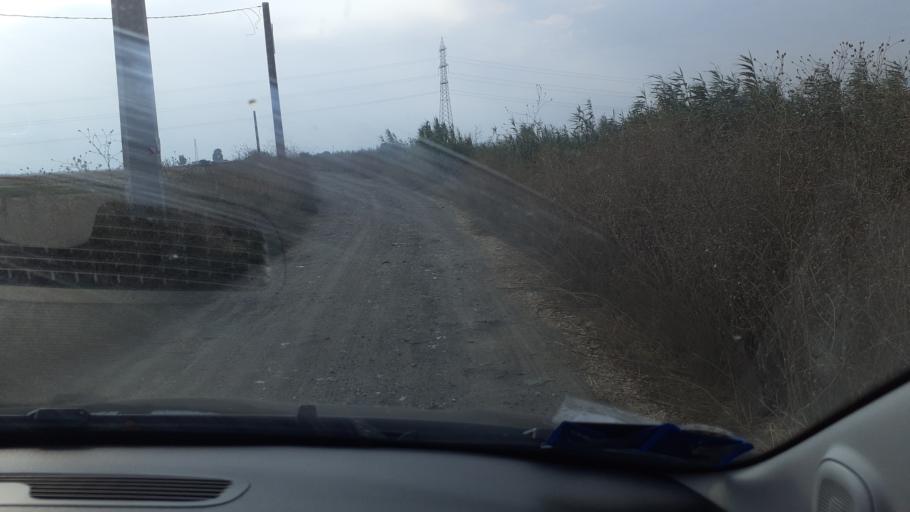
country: IT
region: Sicily
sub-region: Catania
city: Catania
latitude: 37.4325
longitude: 15.0141
